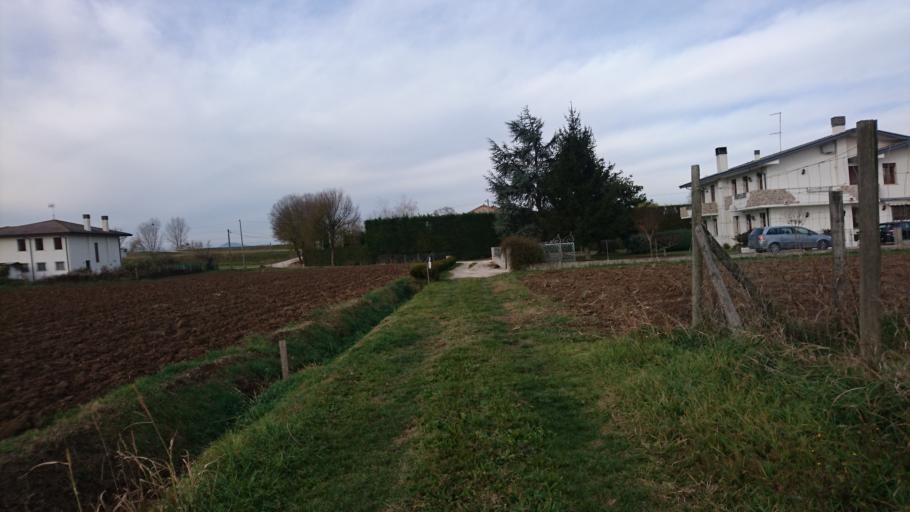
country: IT
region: Veneto
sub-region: Provincia di Padova
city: Polverara
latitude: 45.3156
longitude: 11.9373
